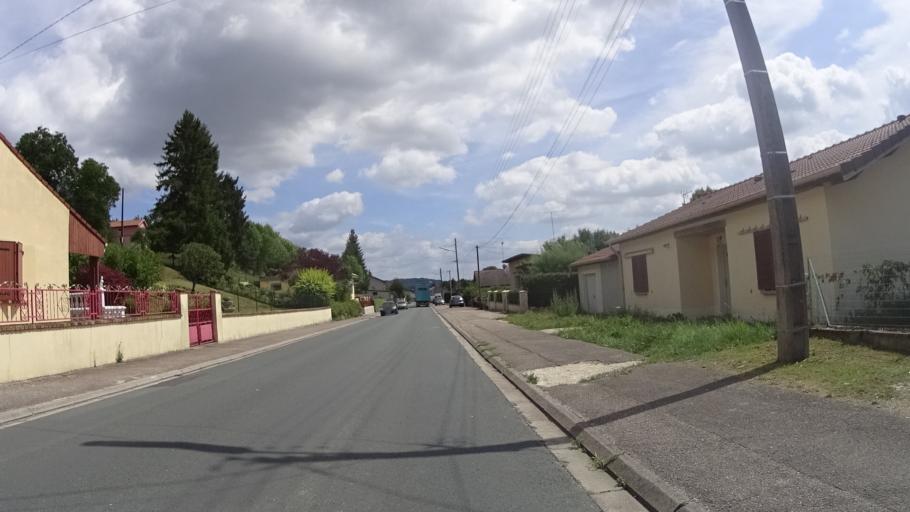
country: FR
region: Lorraine
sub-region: Departement de la Meuse
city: Euville
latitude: 48.7451
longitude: 5.6316
